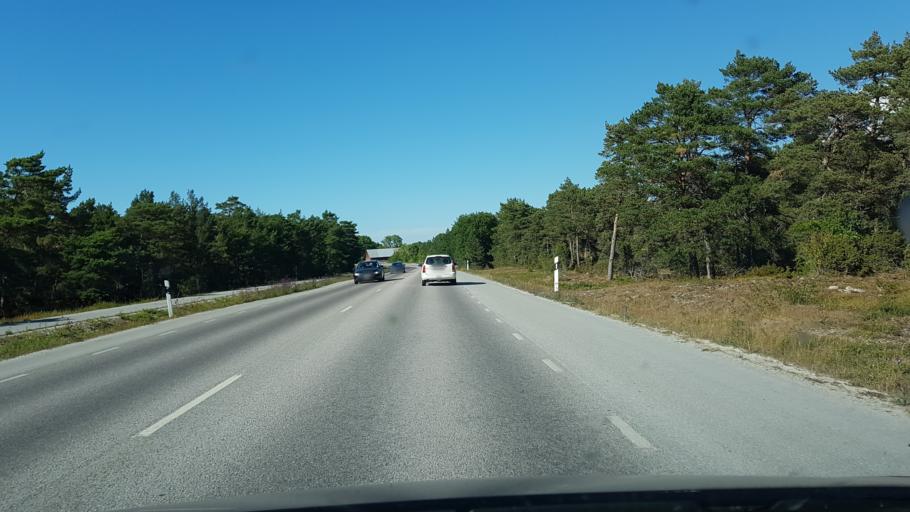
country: SE
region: Gotland
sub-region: Gotland
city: Vibble
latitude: 57.5663
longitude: 18.2069
